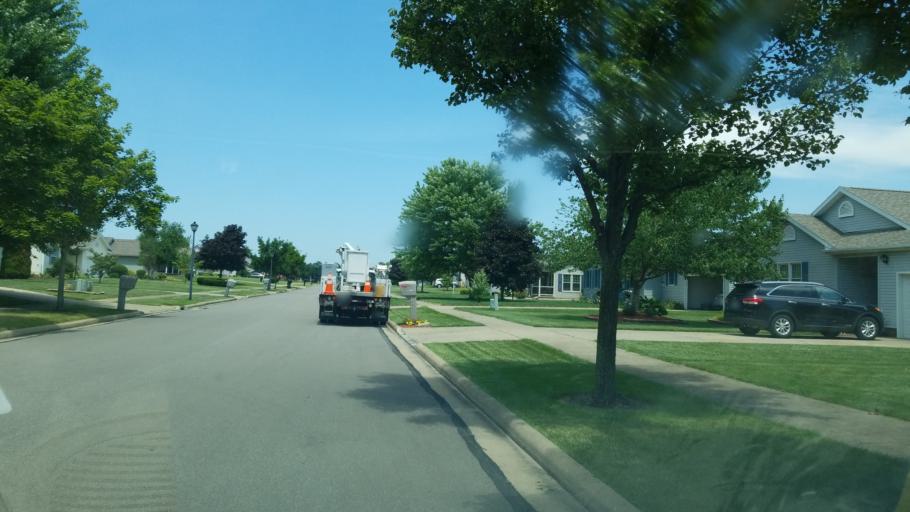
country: US
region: Ohio
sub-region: Ashland County
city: Ashland
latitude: 40.8684
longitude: -82.3388
